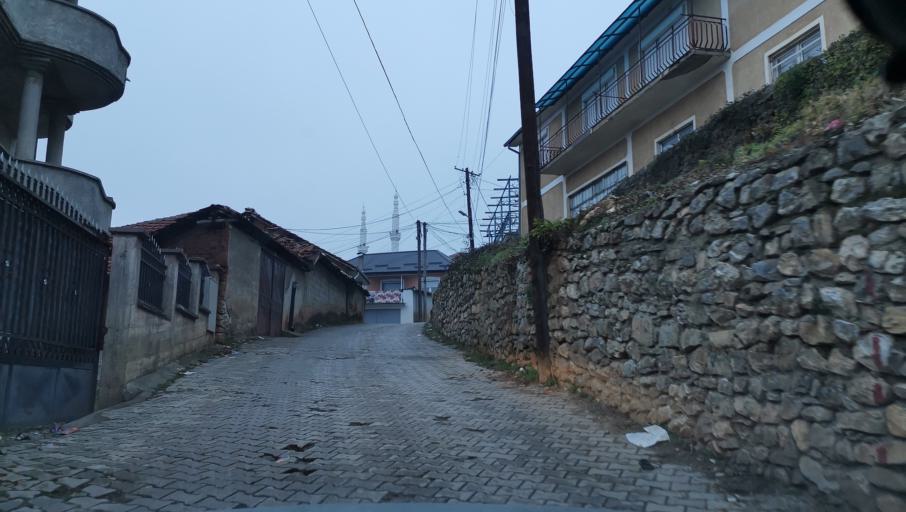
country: MK
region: Debar
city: Debar
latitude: 41.5252
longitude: 20.5280
